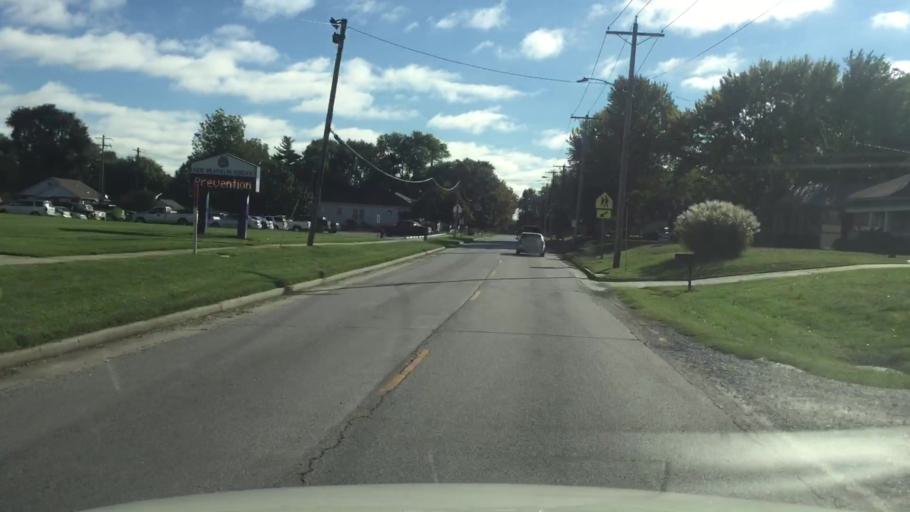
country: US
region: Missouri
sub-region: Howard County
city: New Franklin
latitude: 39.0177
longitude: -92.7428
